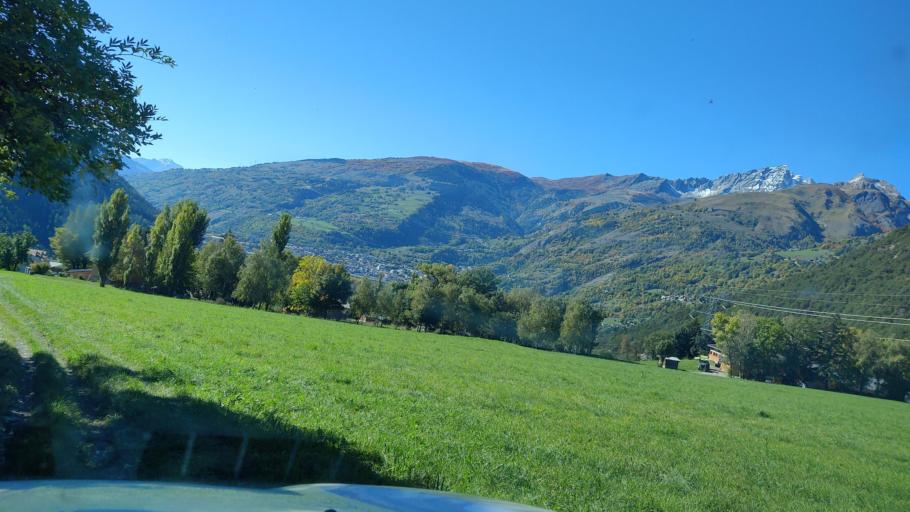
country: FR
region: Rhone-Alpes
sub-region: Departement de la Savoie
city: Seez
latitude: 45.6262
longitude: 6.8073
